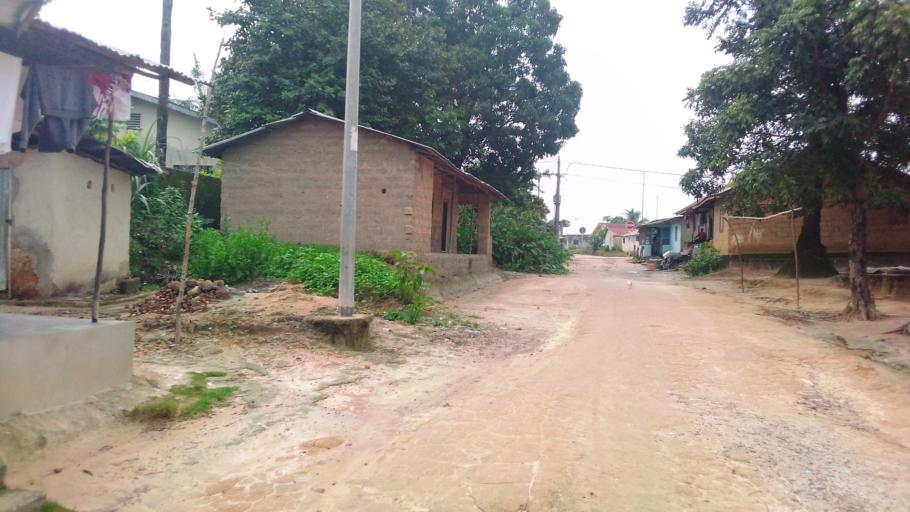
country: SL
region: Northern Province
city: Lunsar
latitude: 8.6861
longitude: -12.5391
